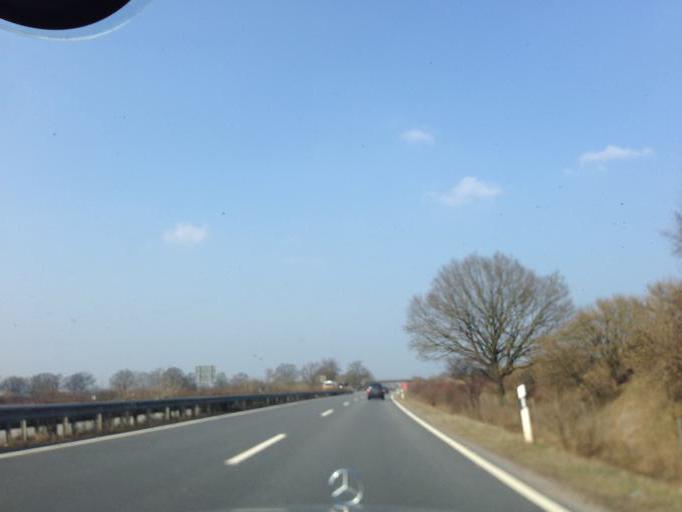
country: DE
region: Schleswig-Holstein
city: Hogersdorf
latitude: 53.9003
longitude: 10.2767
